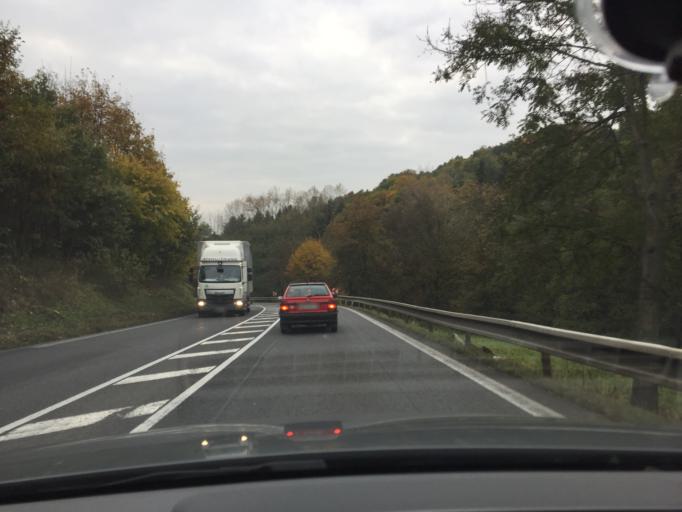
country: CZ
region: Ustecky
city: Rehlovice
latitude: 50.5749
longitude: 13.9363
